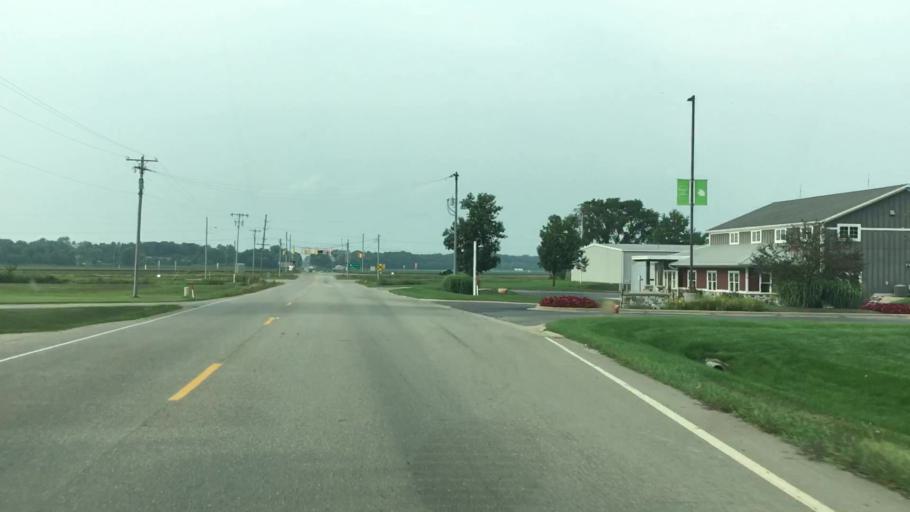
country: US
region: Michigan
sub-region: Ottawa County
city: Hudsonville
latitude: 42.8506
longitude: -85.9006
